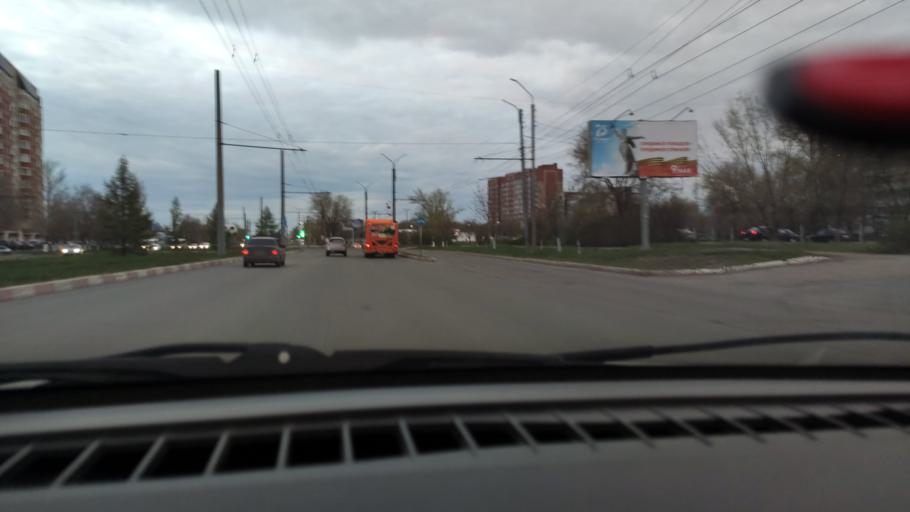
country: RU
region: Orenburg
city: Orenburg
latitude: 51.8165
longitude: 55.1076
